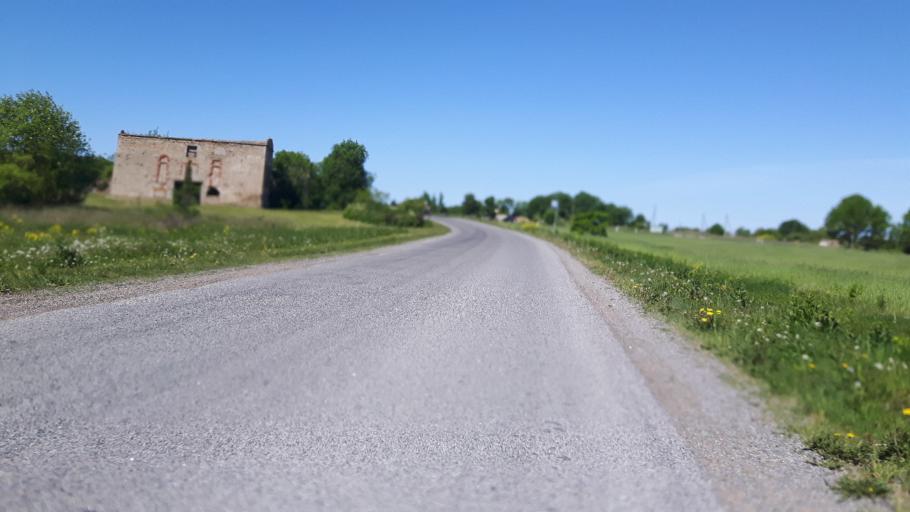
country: EE
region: Ida-Virumaa
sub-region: Sillamaee linn
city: Sillamae
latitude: 59.3860
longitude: 27.8100
